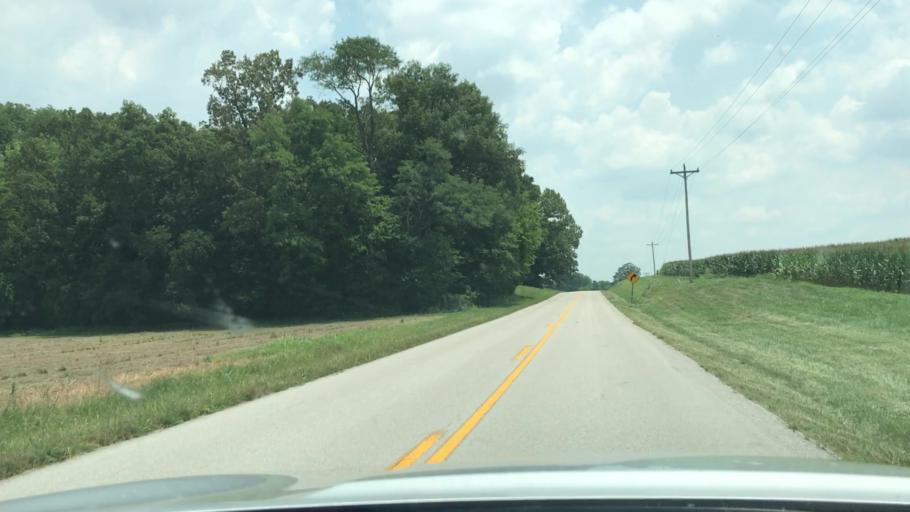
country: US
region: Kentucky
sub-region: Todd County
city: Elkton
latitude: 36.7602
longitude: -87.1007
